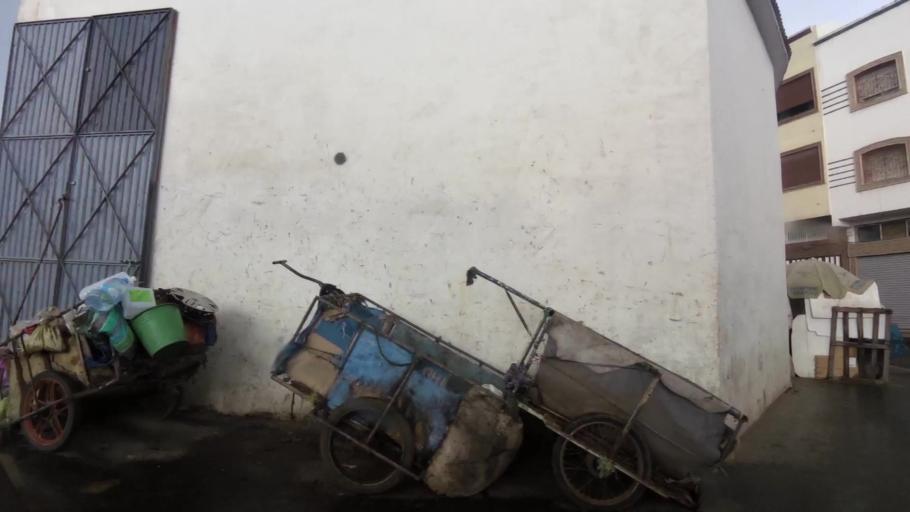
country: MA
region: Grand Casablanca
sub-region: Casablanca
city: Casablanca
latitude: 33.5368
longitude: -7.6694
